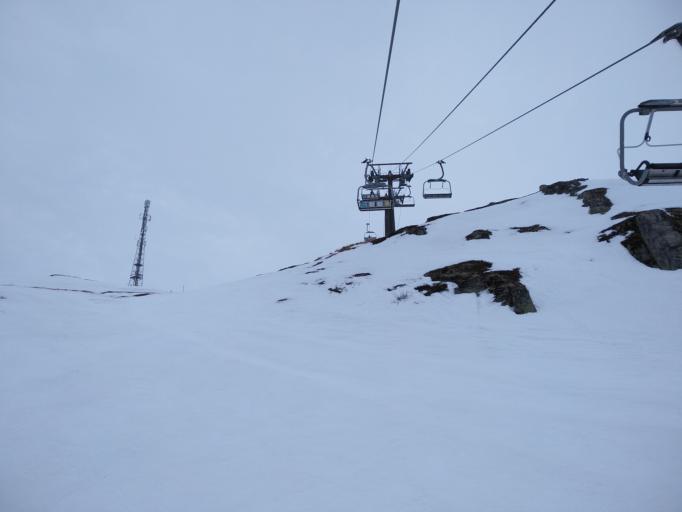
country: NO
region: Aust-Agder
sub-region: Bykle
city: Hovden
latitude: 59.5778
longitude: 7.3351
